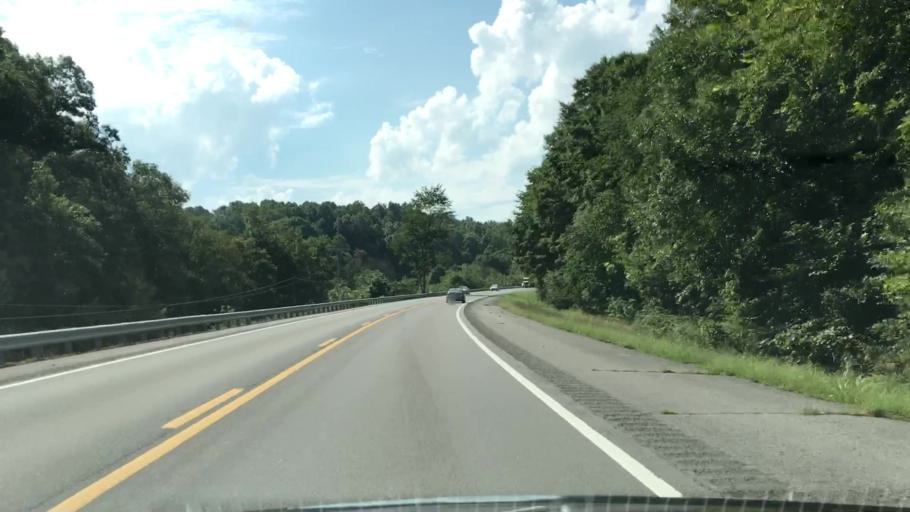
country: US
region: Tennessee
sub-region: Sumner County
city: Westmoreland
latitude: 36.6291
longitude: -86.2388
